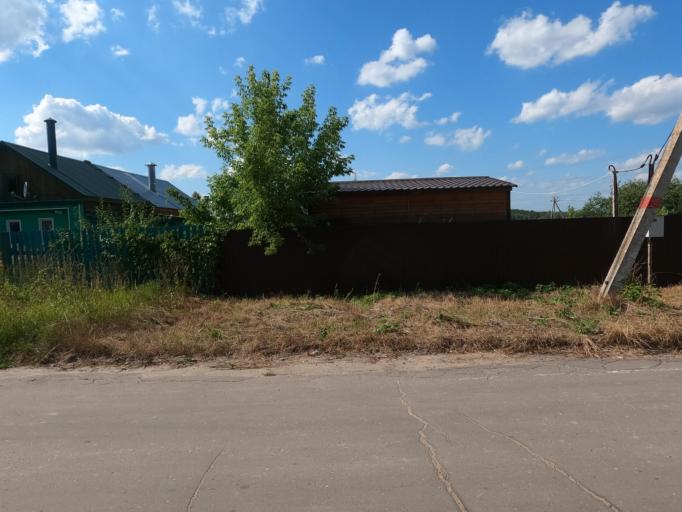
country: RU
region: Moskovskaya
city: Peski
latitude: 55.2318
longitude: 38.7494
